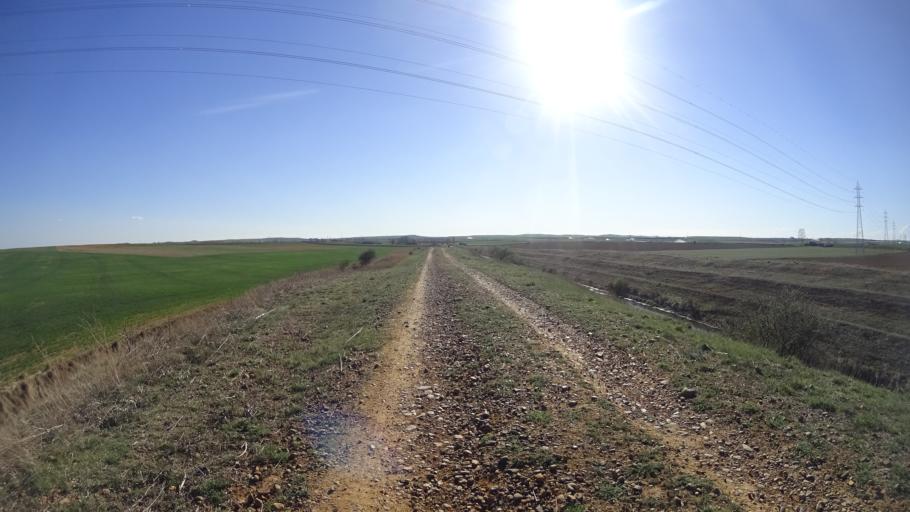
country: ES
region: Castille and Leon
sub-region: Provincia de Palencia
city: Osornillo
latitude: 42.3936
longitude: -4.3523
